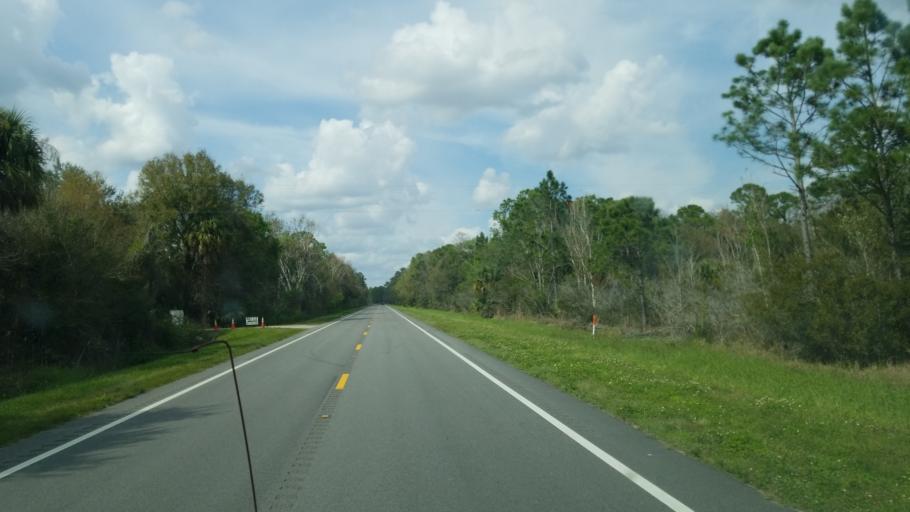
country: US
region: Florida
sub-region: Indian River County
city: Fellsmere
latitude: 27.7872
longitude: -80.9296
